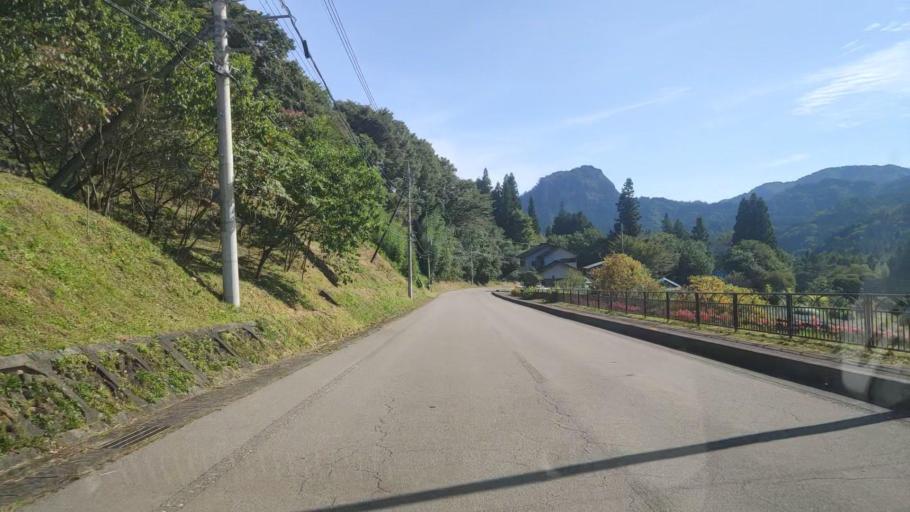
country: JP
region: Gunma
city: Nakanojomachi
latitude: 36.6083
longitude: 138.7256
